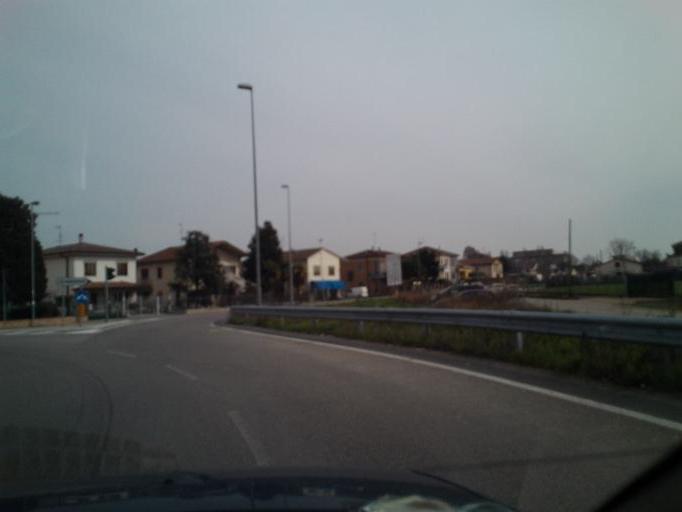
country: IT
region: Lombardy
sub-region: Provincia di Mantova
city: Marmirolo
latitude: 45.2206
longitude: 10.7458
